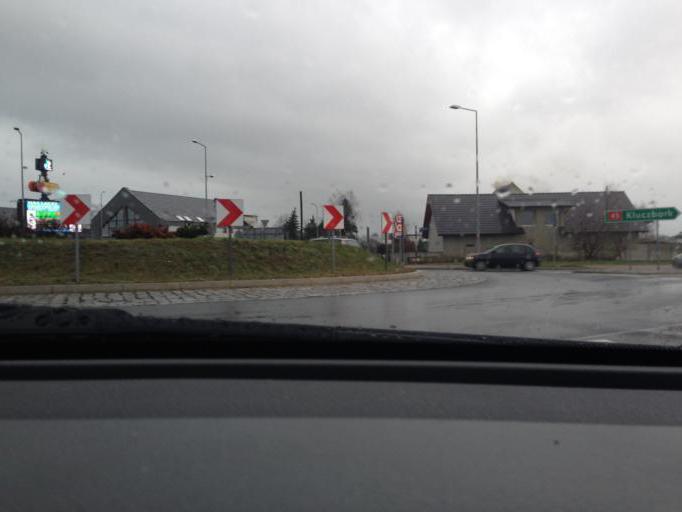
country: PL
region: Opole Voivodeship
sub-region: Powiat opolski
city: Wegry
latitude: 50.7190
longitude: 18.0024
